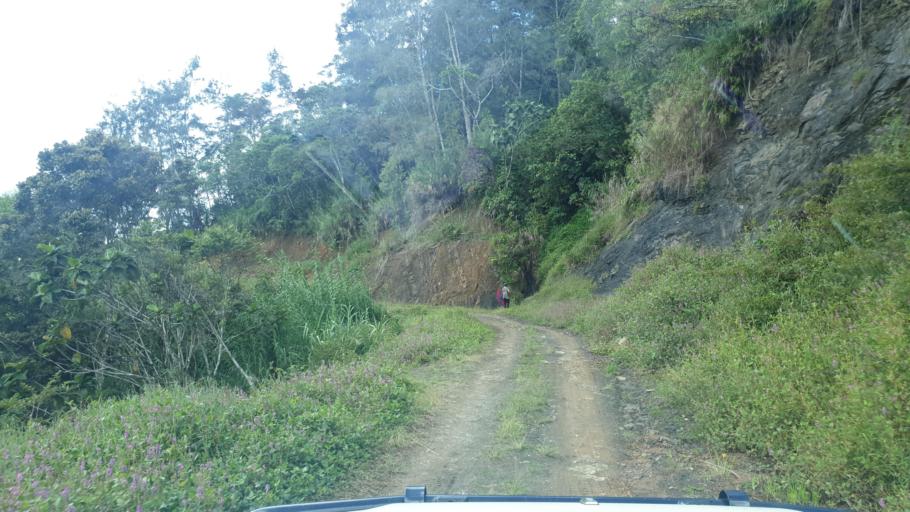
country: PG
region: Eastern Highlands
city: Goroka
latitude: -6.2785
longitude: 145.1894
